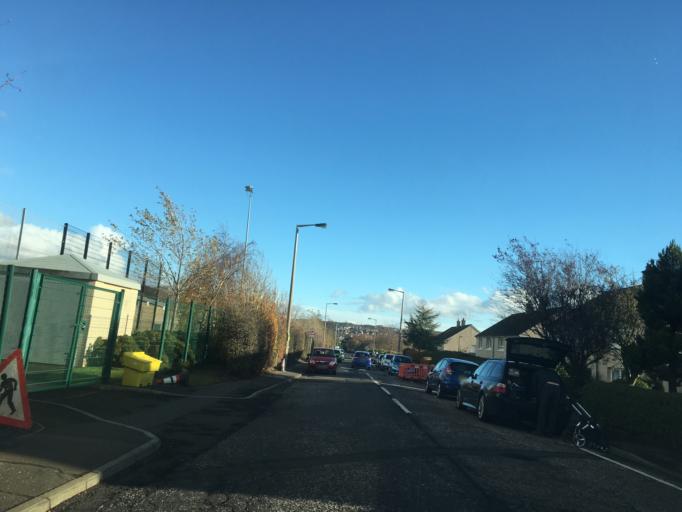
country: GB
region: Scotland
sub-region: Edinburgh
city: Colinton
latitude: 55.9136
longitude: -3.2376
